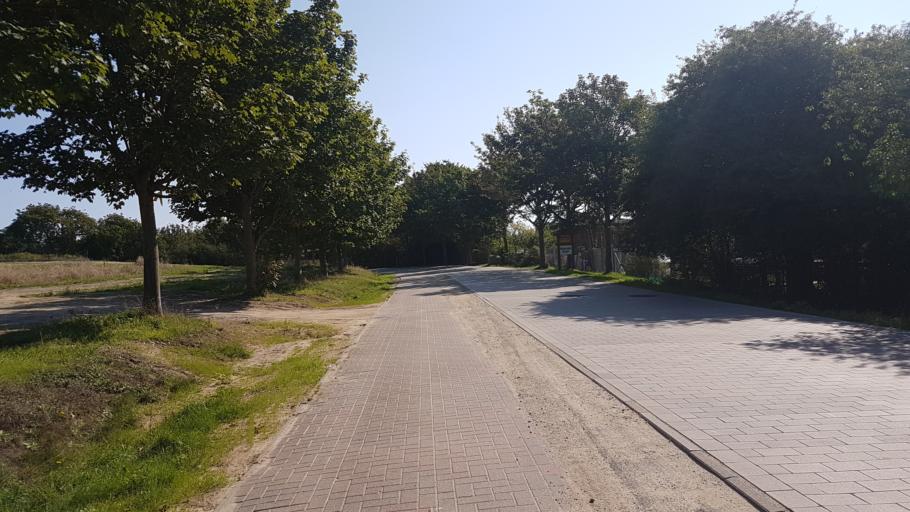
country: DE
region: Mecklenburg-Vorpommern
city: Ostseebad Gohren
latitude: 54.3381
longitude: 13.7300
